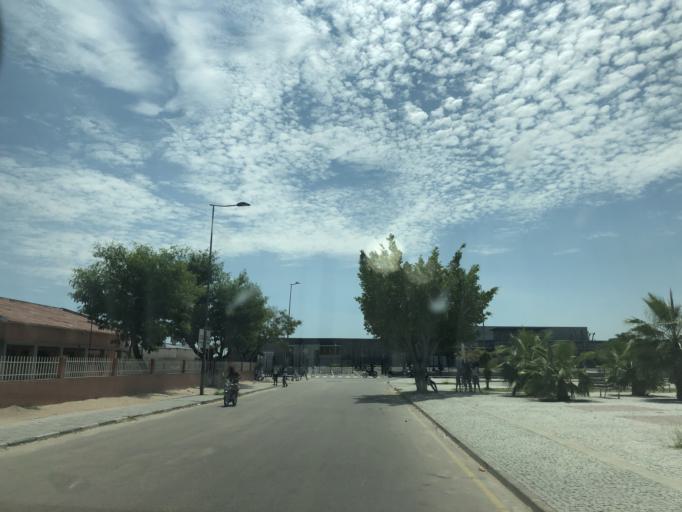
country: AO
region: Cunene
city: Ondjiva
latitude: -17.0658
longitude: 15.7284
